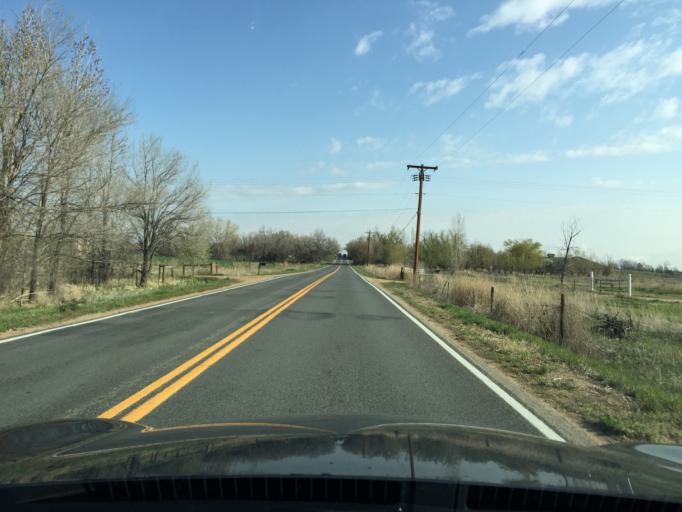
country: US
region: Colorado
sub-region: Boulder County
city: Erie
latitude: 40.0962
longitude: -105.0554
